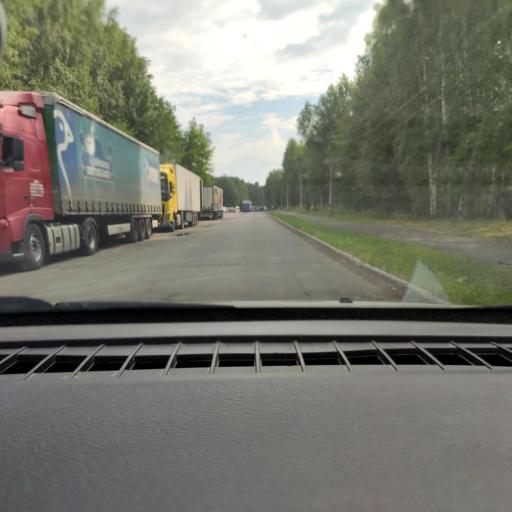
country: RU
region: Perm
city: Overyata
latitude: 58.0174
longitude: 55.9224
